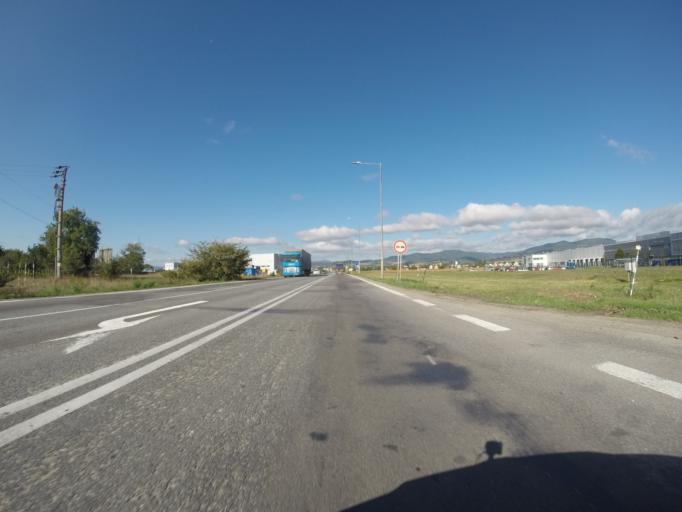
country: SK
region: Trenciansky
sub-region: Okres Trencin
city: Trencin
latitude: 48.8483
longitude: 17.9947
